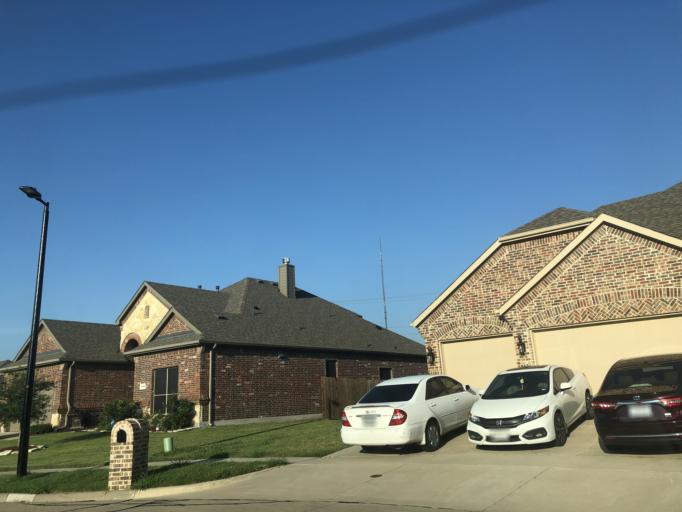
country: US
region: Texas
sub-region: Dallas County
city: Sunnyvale
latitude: 32.8457
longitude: -96.5599
